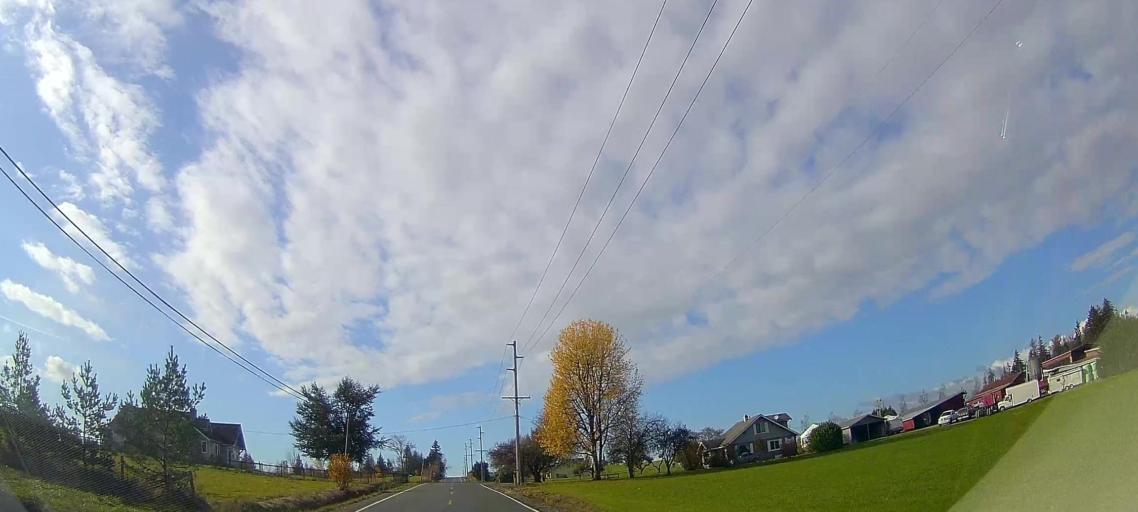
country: US
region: Washington
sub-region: Skagit County
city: Clear Lake
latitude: 48.4352
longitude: -122.2502
